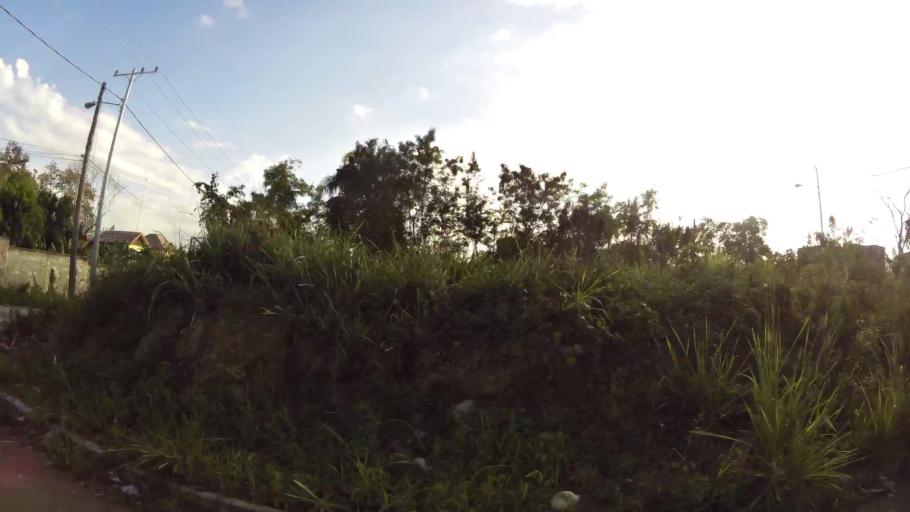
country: DO
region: Nacional
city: Ensanche Luperon
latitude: 18.5474
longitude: -69.9136
